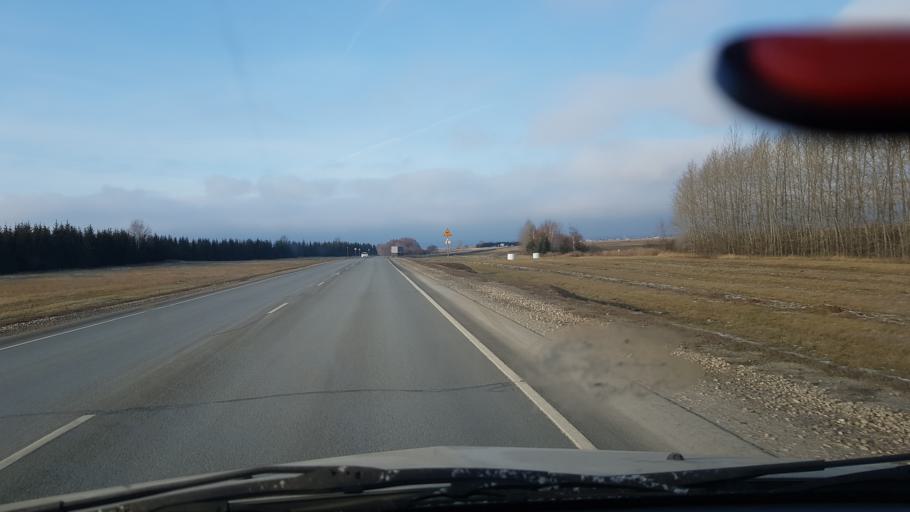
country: RU
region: Tatarstan
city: Laishevo
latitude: 55.3971
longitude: 49.7729
